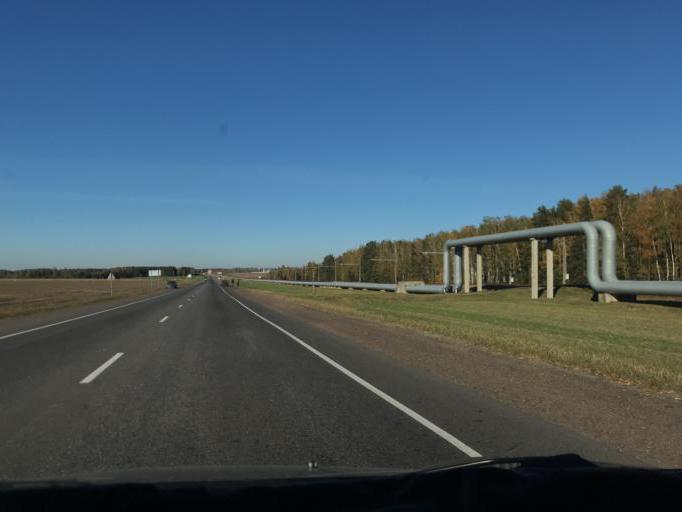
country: BY
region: Gomel
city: Mazyr
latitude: 51.9807
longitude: 29.2602
